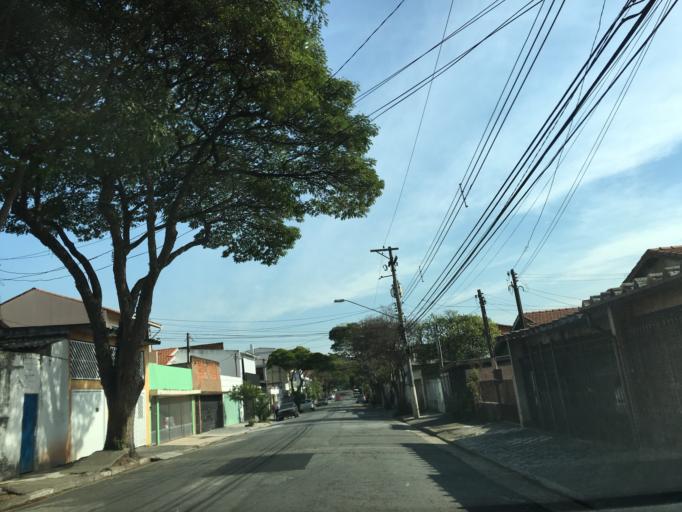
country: BR
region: Sao Paulo
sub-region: Osasco
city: Osasco
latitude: -23.5766
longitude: -46.7260
